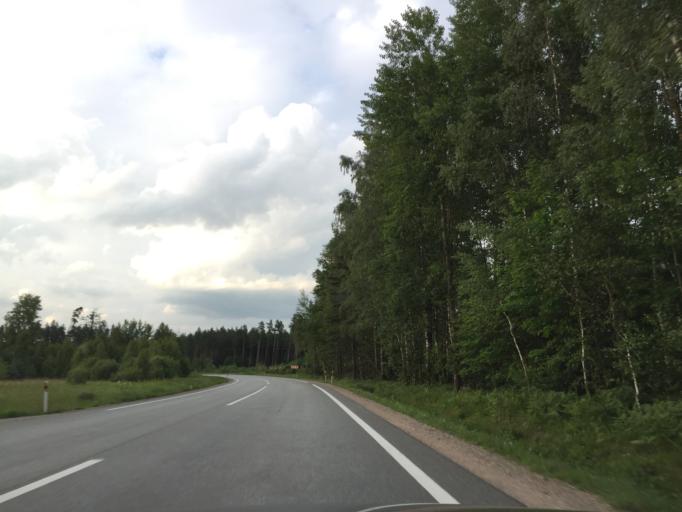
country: LV
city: Tireli
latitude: 56.8639
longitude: 23.6189
